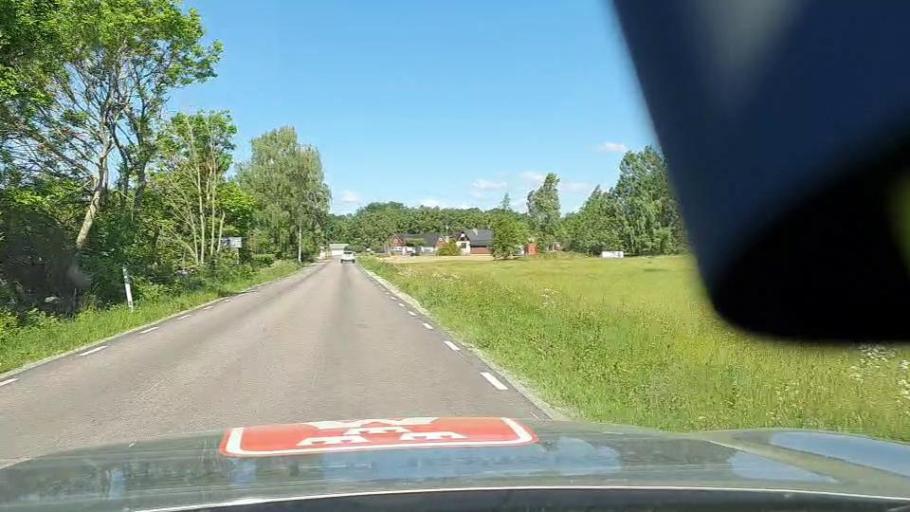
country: SE
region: Blekinge
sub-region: Solvesborgs Kommun
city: Soelvesborg
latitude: 56.0151
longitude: 14.7202
